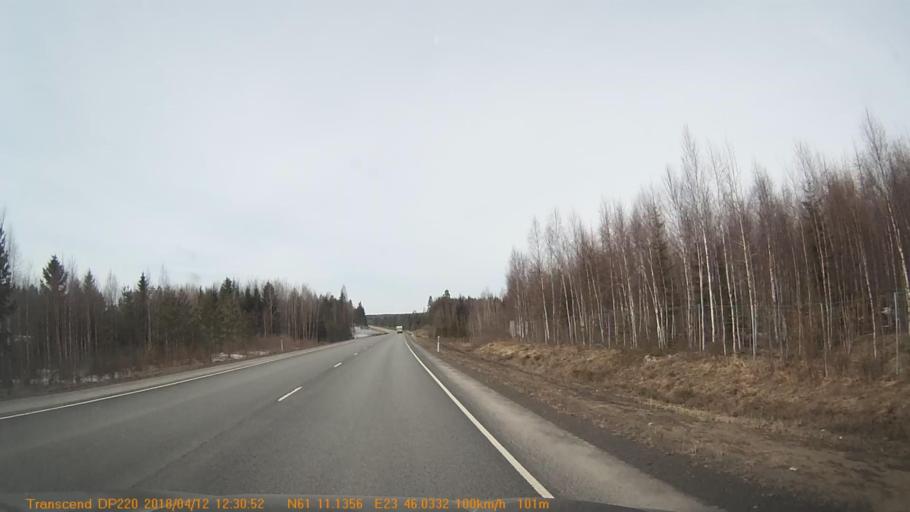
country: FI
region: Pirkanmaa
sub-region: Etelae-Pirkanmaa
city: Viiala
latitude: 61.1857
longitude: 23.7667
